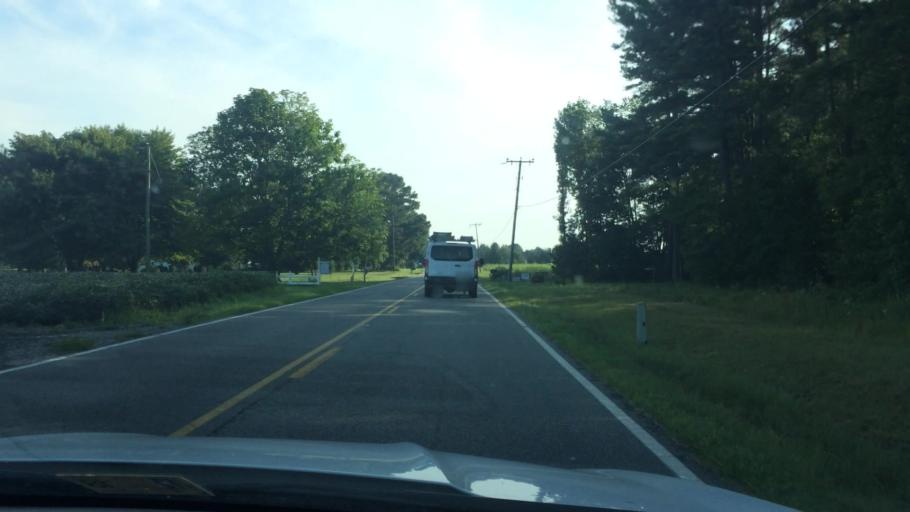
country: US
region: Virginia
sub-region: Gloucester County
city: Gloucester Courthouse
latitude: 37.4841
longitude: -76.4427
